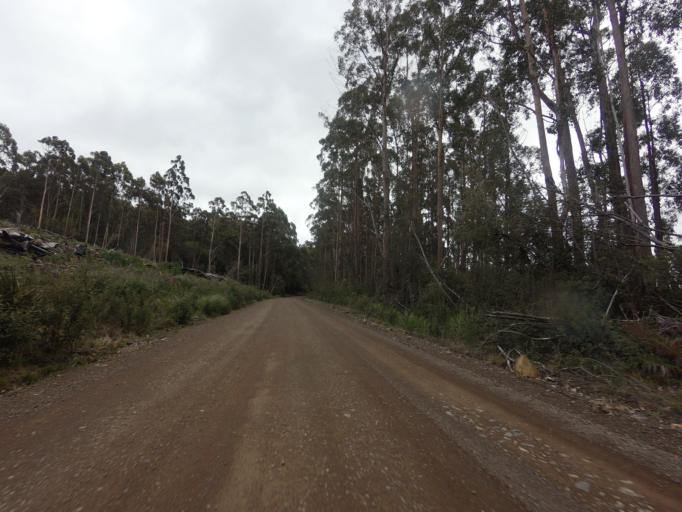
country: AU
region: Tasmania
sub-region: Huon Valley
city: Geeveston
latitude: -43.4865
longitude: 146.8914
